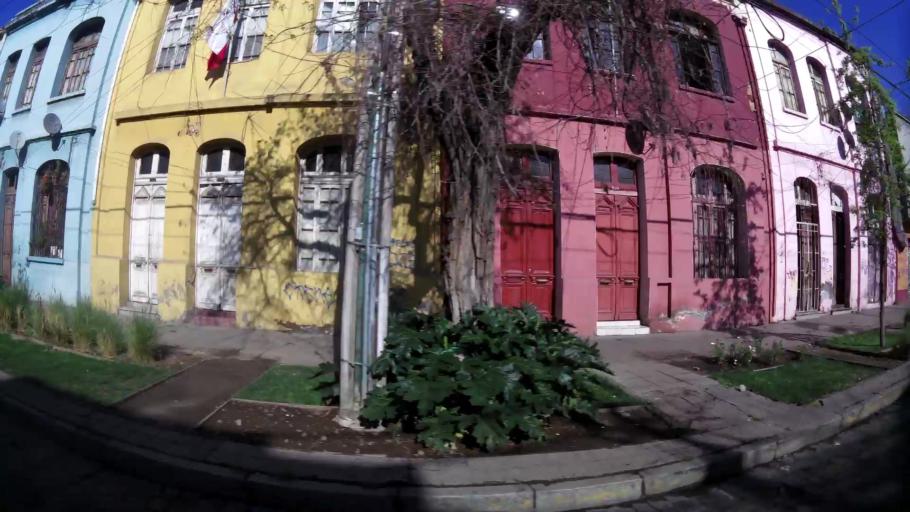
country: CL
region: Santiago Metropolitan
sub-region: Provincia de Santiago
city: Santiago
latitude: -33.4583
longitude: -70.6329
